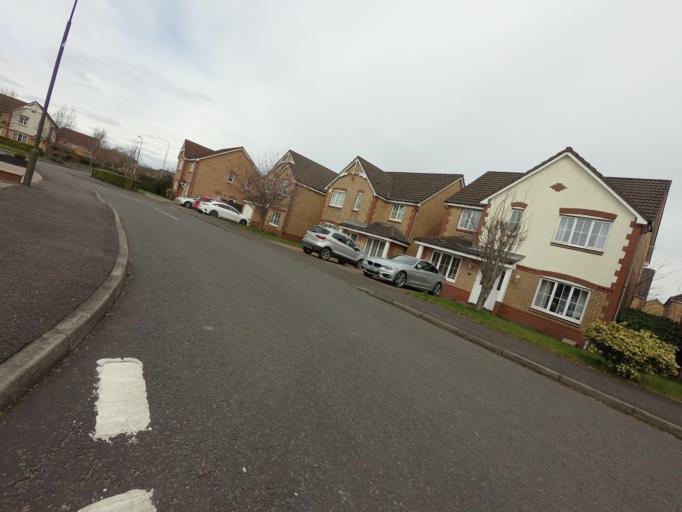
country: GB
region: Scotland
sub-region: West Lothian
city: Broxburn
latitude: 55.9300
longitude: -3.4809
